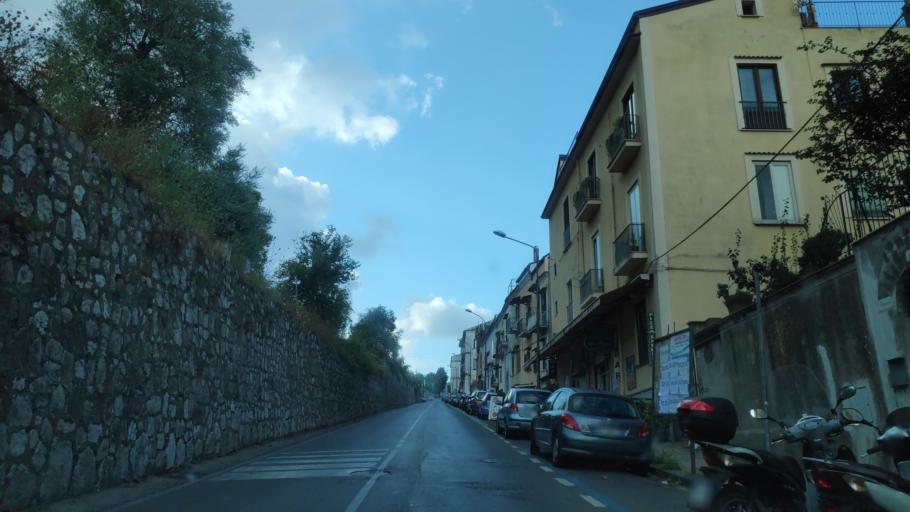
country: IT
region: Campania
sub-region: Provincia di Napoli
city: Piano di Sorrento
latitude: 40.6329
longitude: 14.4184
